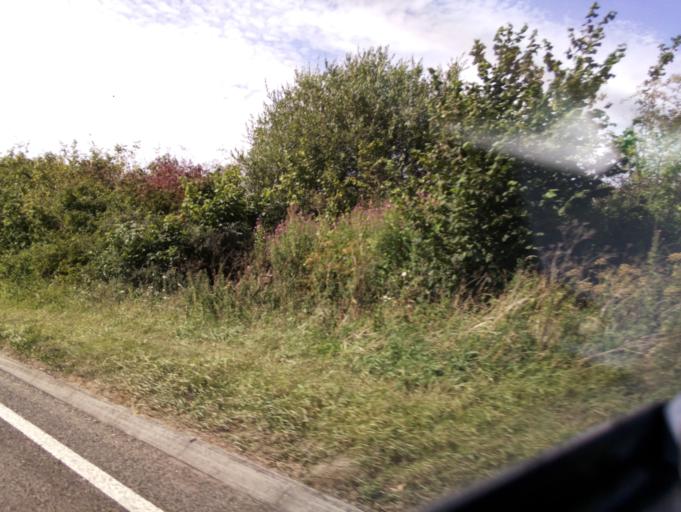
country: GB
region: England
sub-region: Dorset
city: Lytchett Matravers
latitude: 50.7339
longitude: -2.0738
